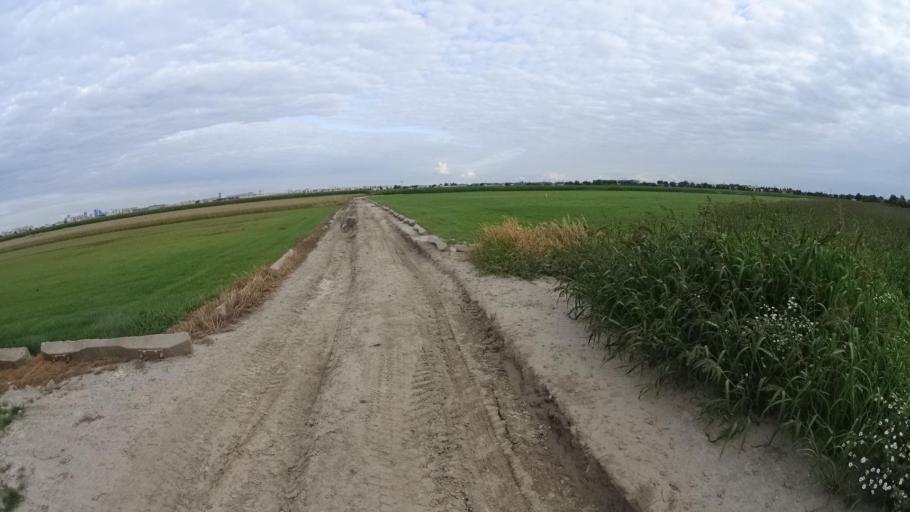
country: PL
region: Masovian Voivodeship
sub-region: Powiat warszawski zachodni
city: Babice
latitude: 52.2383
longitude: 20.8674
